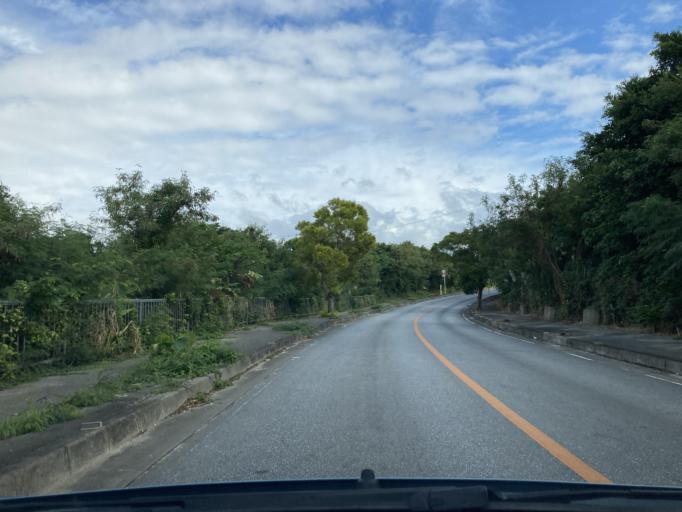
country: JP
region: Okinawa
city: Itoman
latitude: 26.1310
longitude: 127.7090
